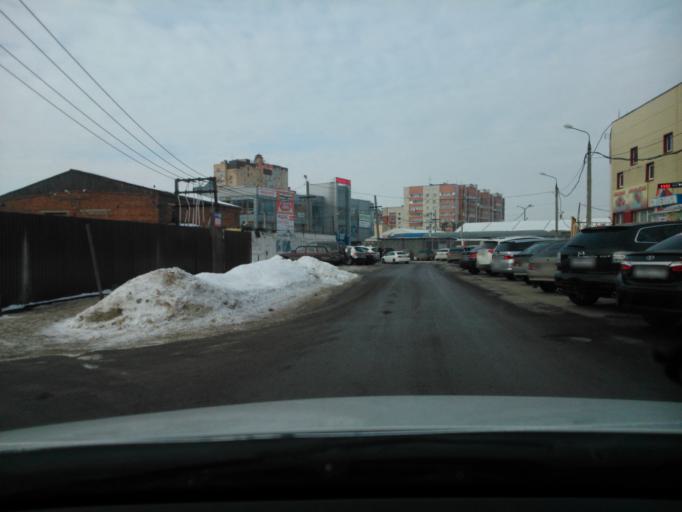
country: RU
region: Perm
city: Perm
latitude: 58.0013
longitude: 56.2247
